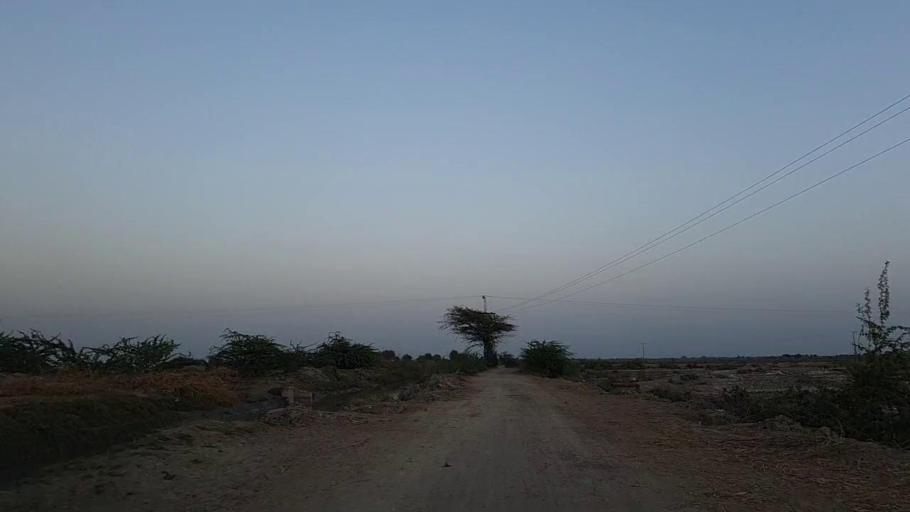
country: PK
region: Sindh
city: Pithoro
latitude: 25.4152
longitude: 69.3113
